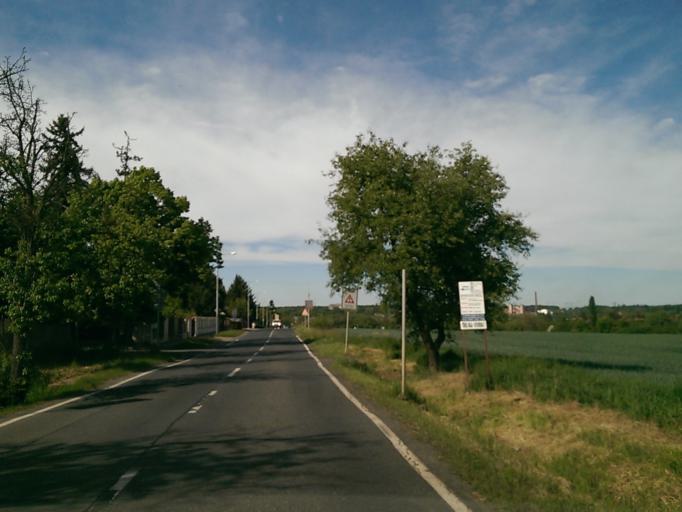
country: CZ
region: Praha
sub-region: Praha 14
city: Dolni Pocernice
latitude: 50.0752
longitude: 14.6027
